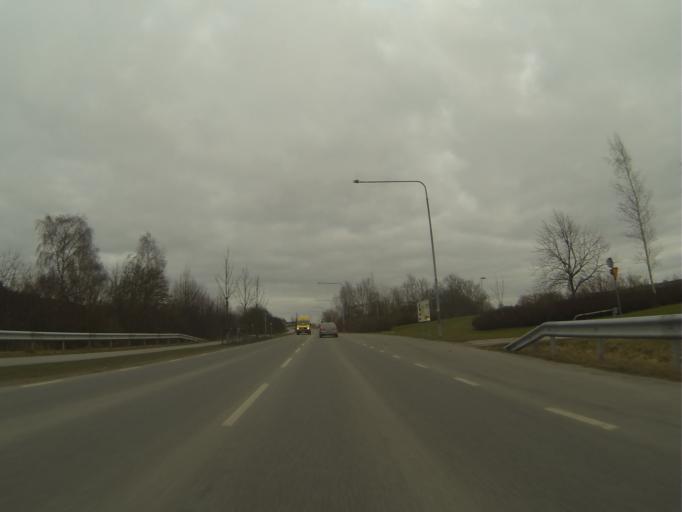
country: SE
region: Skane
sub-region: Svedala Kommun
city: Svedala
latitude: 55.5167
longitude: 13.2288
